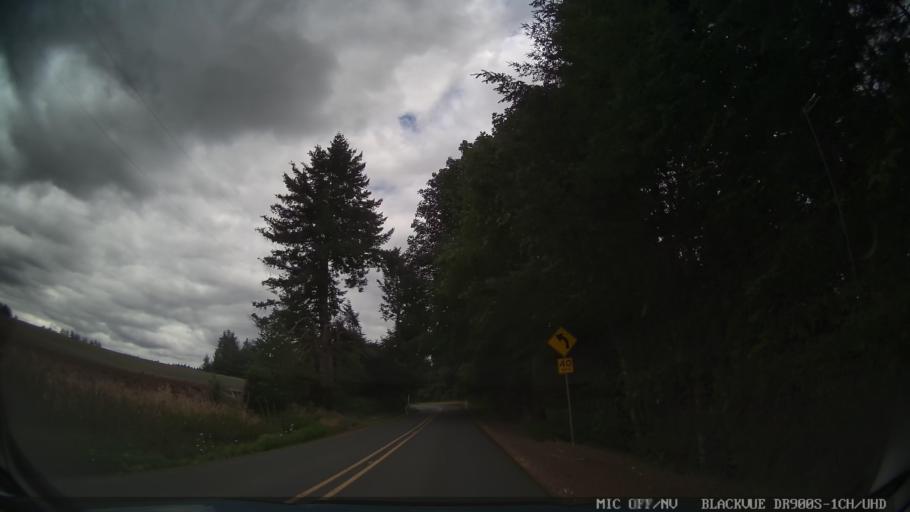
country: US
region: Oregon
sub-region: Linn County
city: Lyons
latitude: 44.8499
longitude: -122.6751
